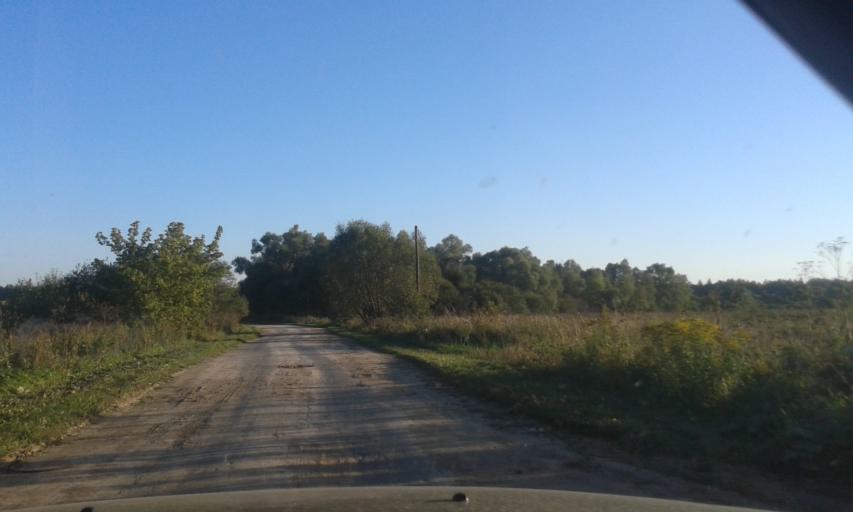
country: RU
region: Tula
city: Krapivna
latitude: 54.1221
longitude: 37.1533
